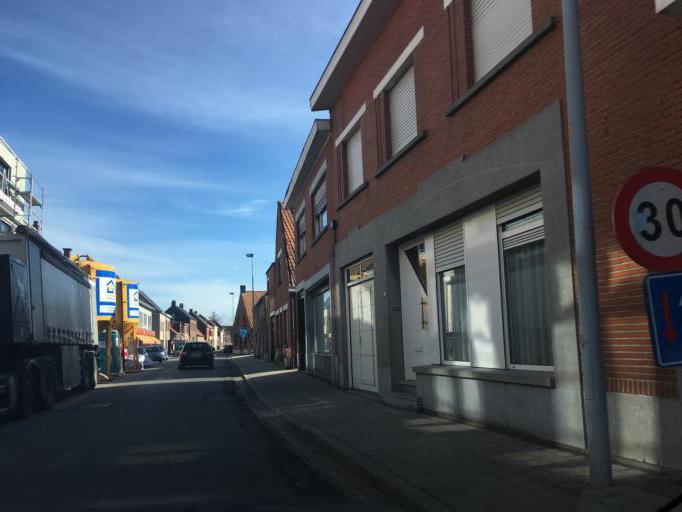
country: BE
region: Flanders
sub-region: Provincie West-Vlaanderen
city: Ledegem
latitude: 50.8556
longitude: 3.1283
